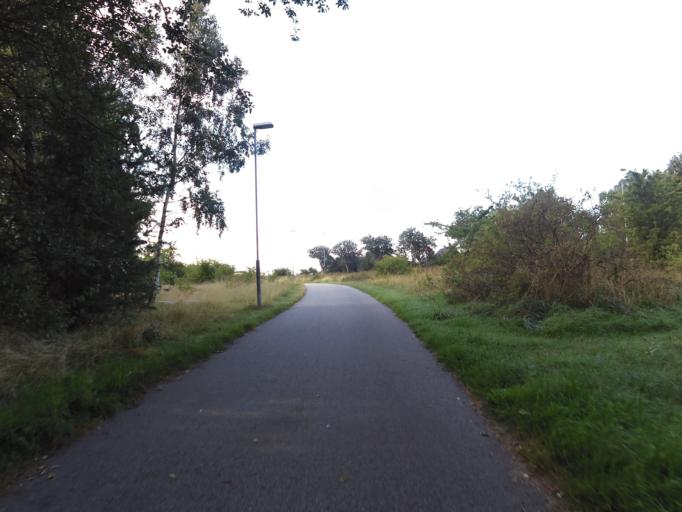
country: SE
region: Skane
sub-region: Lomma Kommun
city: Lomma
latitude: 55.6876
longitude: 13.0629
